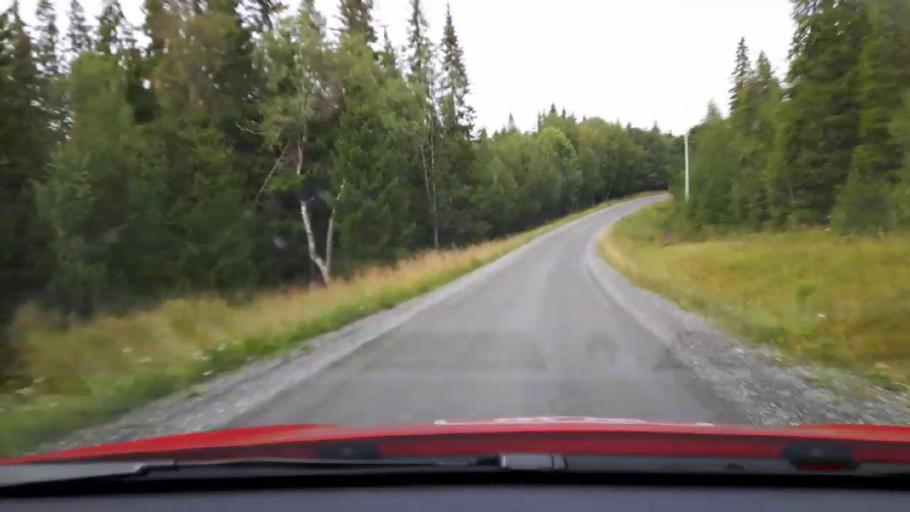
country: SE
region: Jaemtland
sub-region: Are Kommun
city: Are
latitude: 63.7693
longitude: 13.0919
